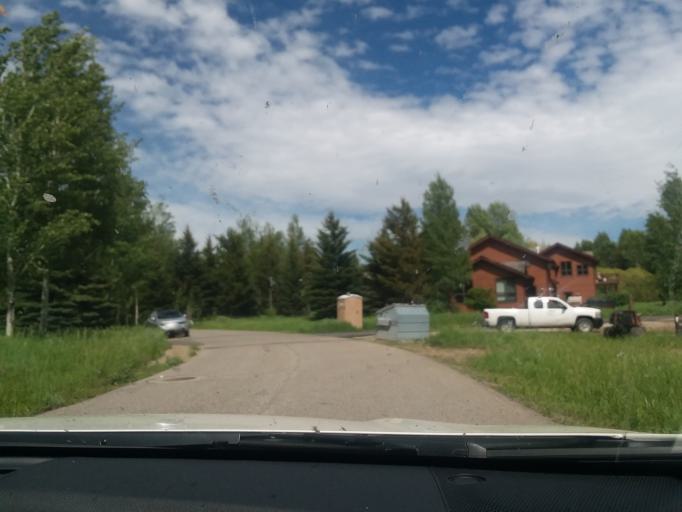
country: US
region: Wyoming
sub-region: Teton County
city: Moose Wilson Road
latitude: 43.5035
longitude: -110.8519
